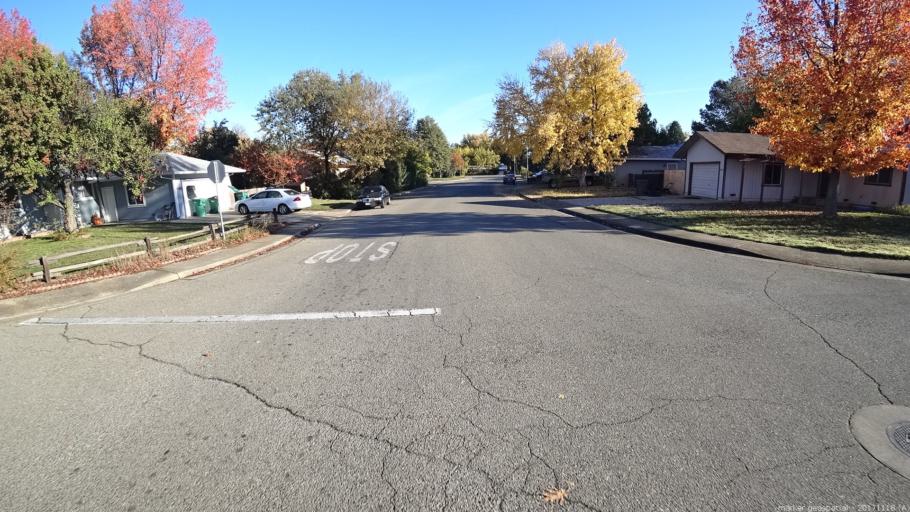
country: US
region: California
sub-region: Shasta County
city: Anderson
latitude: 40.4551
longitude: -122.2827
